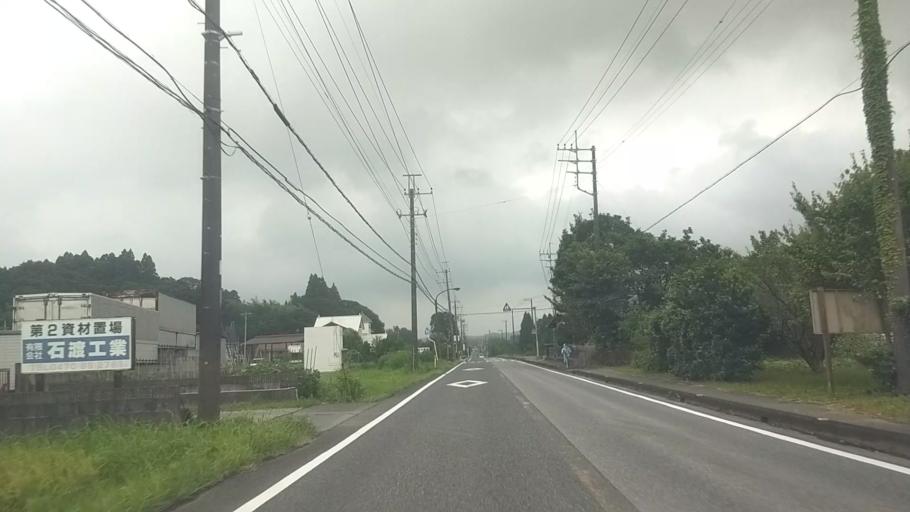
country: JP
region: Chiba
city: Ohara
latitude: 35.2847
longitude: 140.2706
